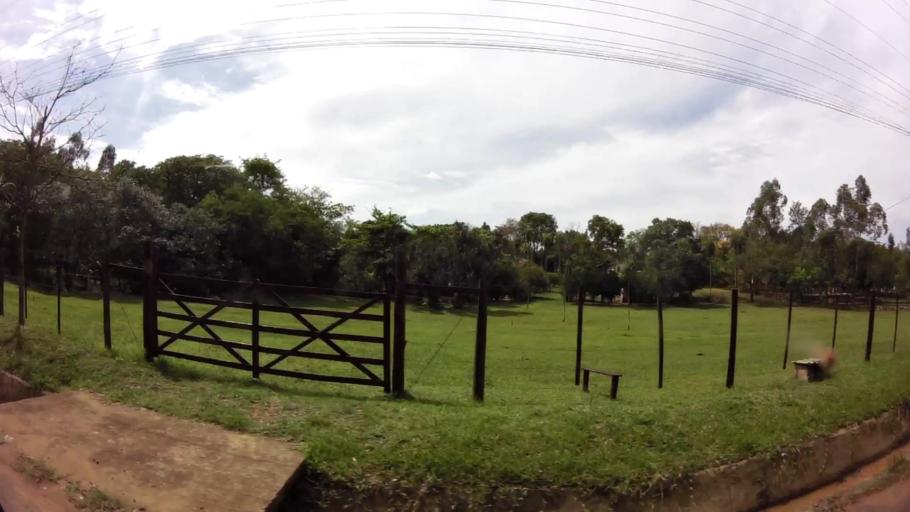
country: PY
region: Central
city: Limpio
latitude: -25.1790
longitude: -57.4426
